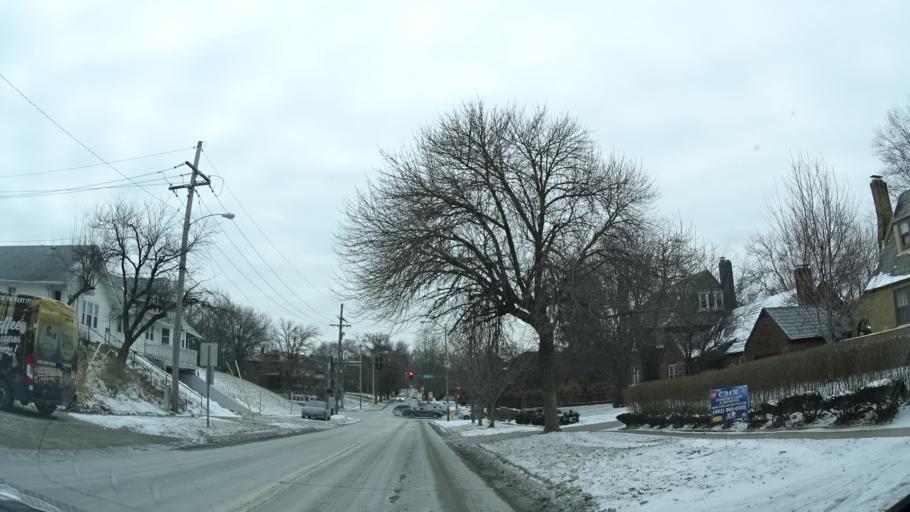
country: US
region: Nebraska
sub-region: Douglas County
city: Omaha
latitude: 41.2604
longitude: -95.9952
